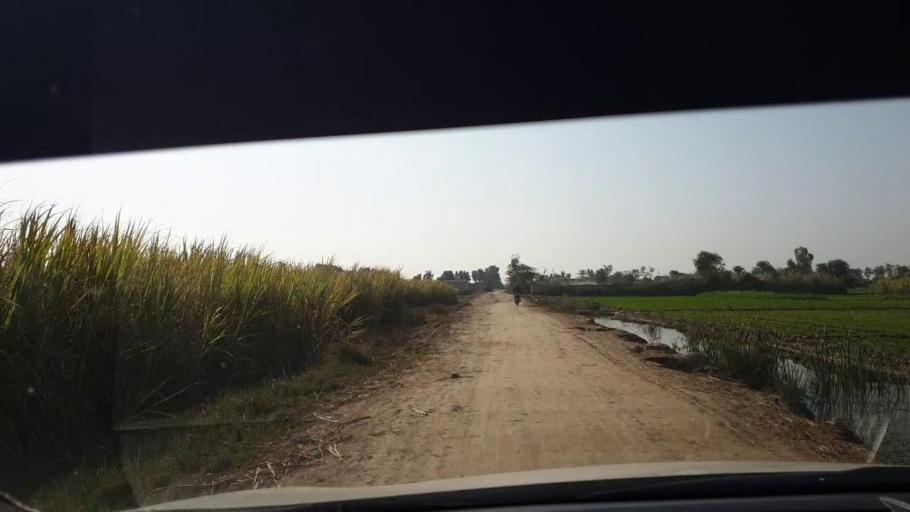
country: PK
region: Sindh
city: Berani
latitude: 25.8025
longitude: 68.8952
